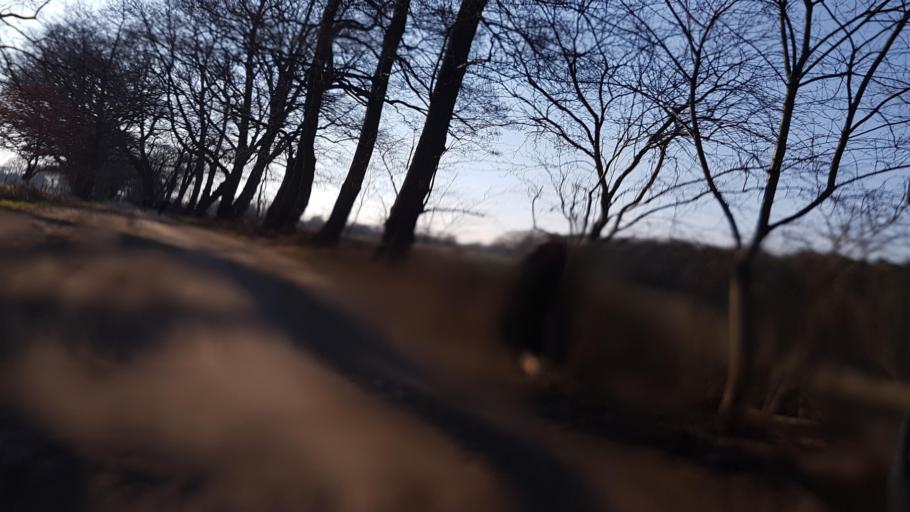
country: DE
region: Lower Saxony
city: Garbsen-Mitte
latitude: 52.4510
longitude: 9.6374
